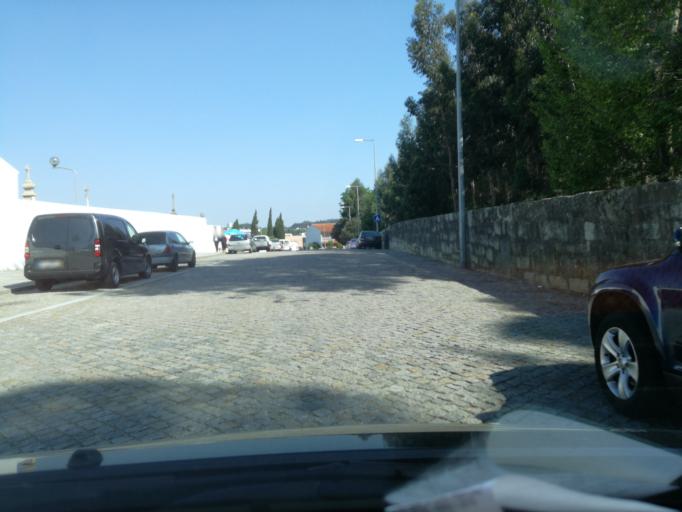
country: PT
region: Porto
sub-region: Maia
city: Maia
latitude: 41.2350
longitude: -8.6298
